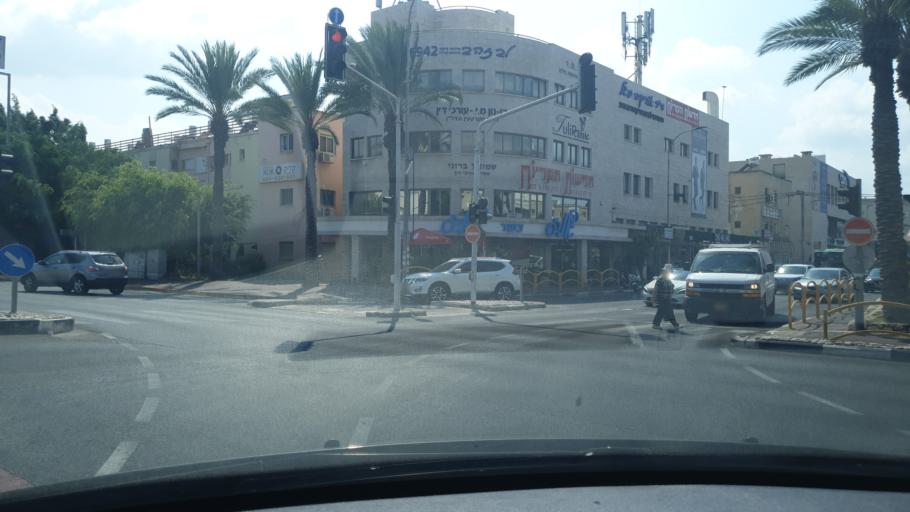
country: IL
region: Haifa
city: Qiryat Bialik
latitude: 32.8242
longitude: 35.0797
